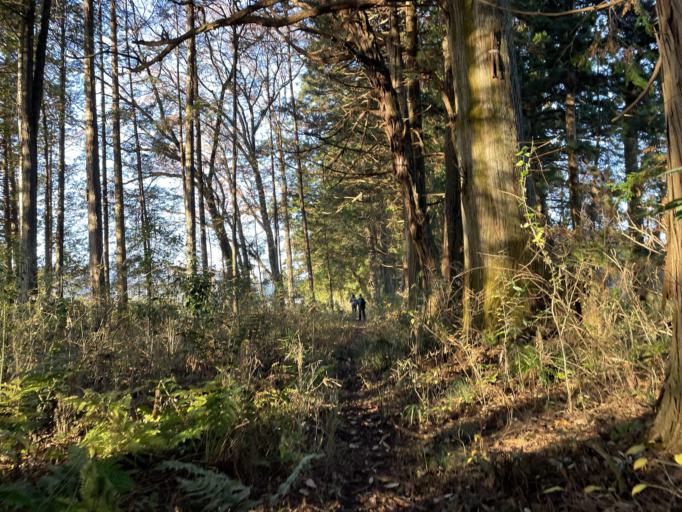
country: JP
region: Tochigi
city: Imaichi
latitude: 36.6579
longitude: 139.7215
